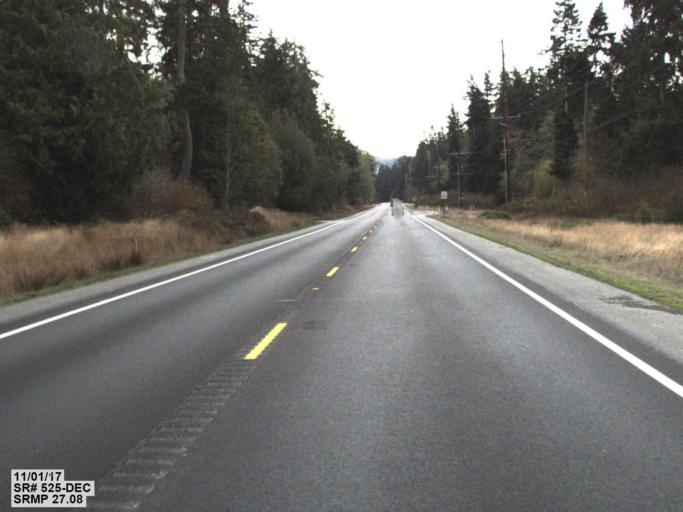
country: US
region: Washington
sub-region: Island County
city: Camano
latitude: 48.1247
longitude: -122.5885
